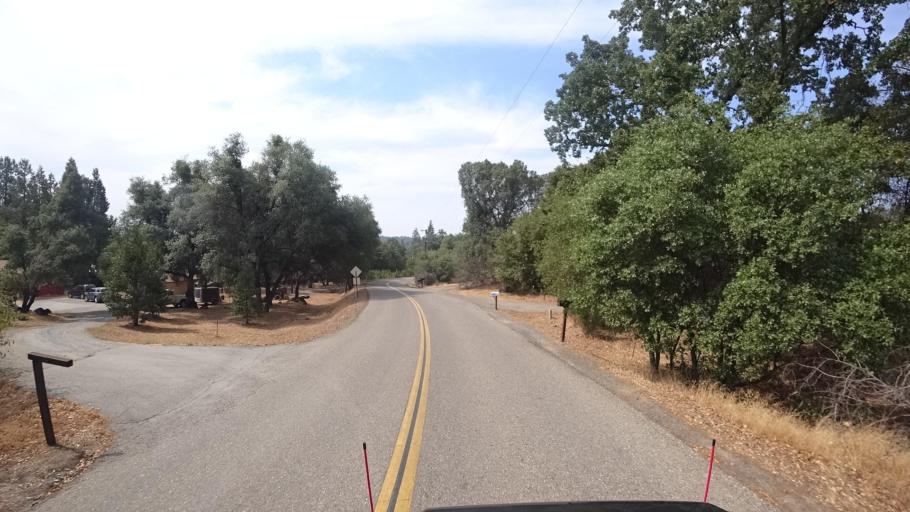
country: US
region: California
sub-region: Mariposa County
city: Midpines
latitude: 37.4999
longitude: -119.9075
